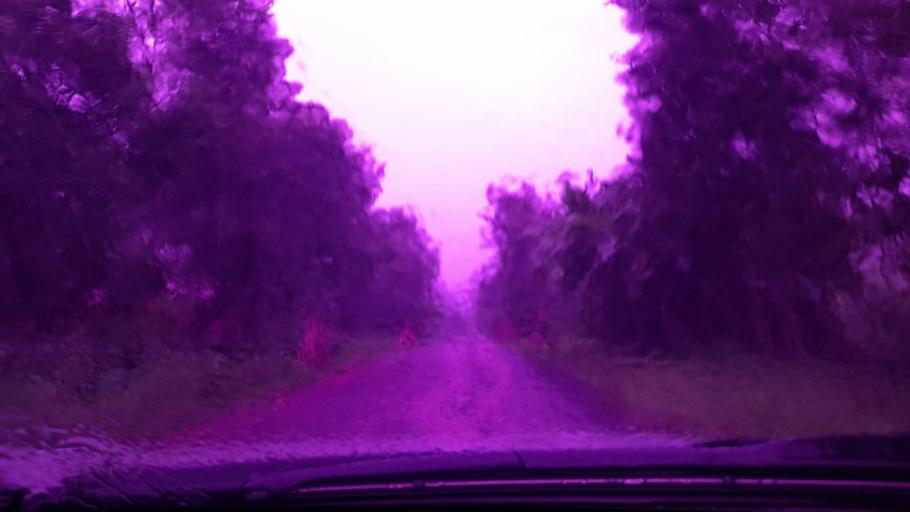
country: ET
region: Oromiya
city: Metu
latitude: 8.4661
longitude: 35.6397
